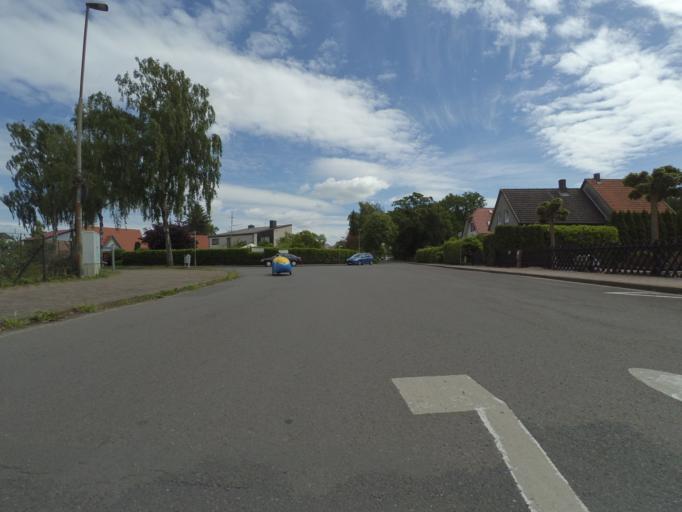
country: DE
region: Lower Saxony
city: Hagenburg
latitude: 52.4581
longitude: 9.3606
